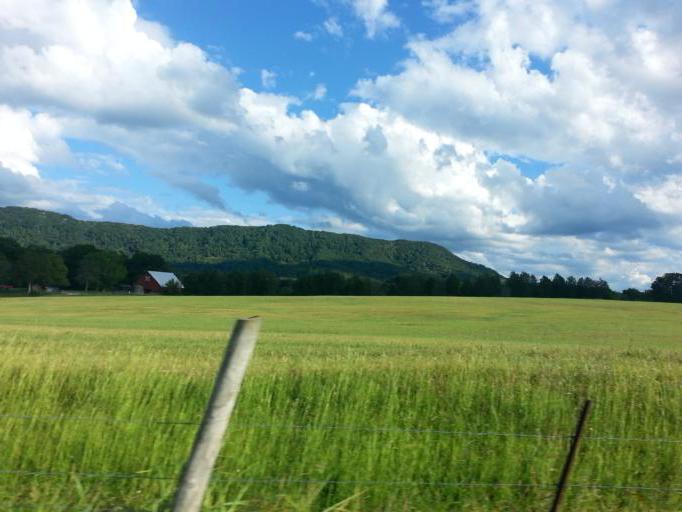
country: US
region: Tennessee
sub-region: Union County
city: Condon
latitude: 36.1279
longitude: -83.7882
